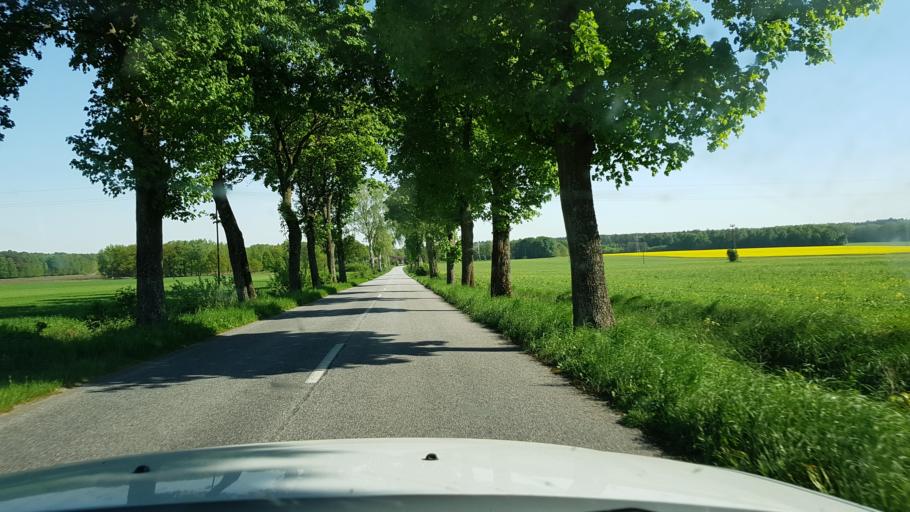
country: PL
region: West Pomeranian Voivodeship
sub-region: Powiat lobeski
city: Resko
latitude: 53.8269
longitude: 15.3915
